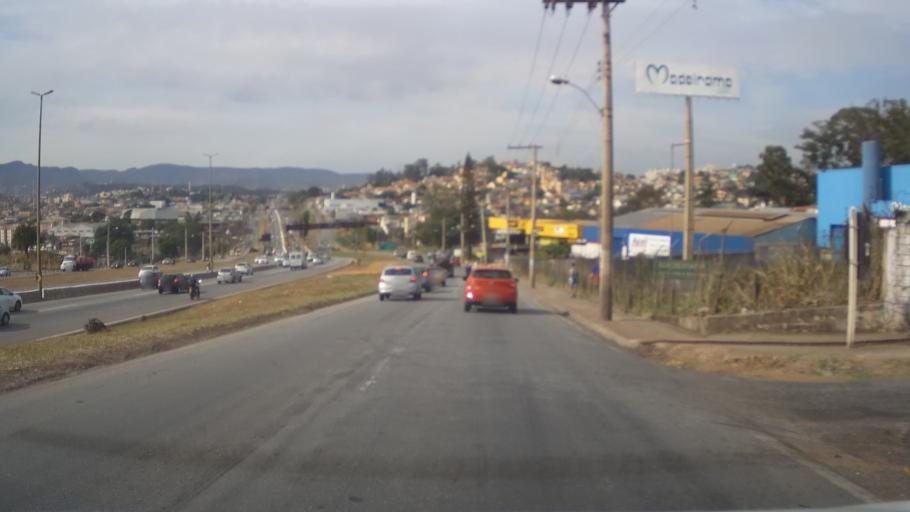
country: BR
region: Minas Gerais
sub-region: Contagem
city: Contagem
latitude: -19.9287
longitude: -44.0071
